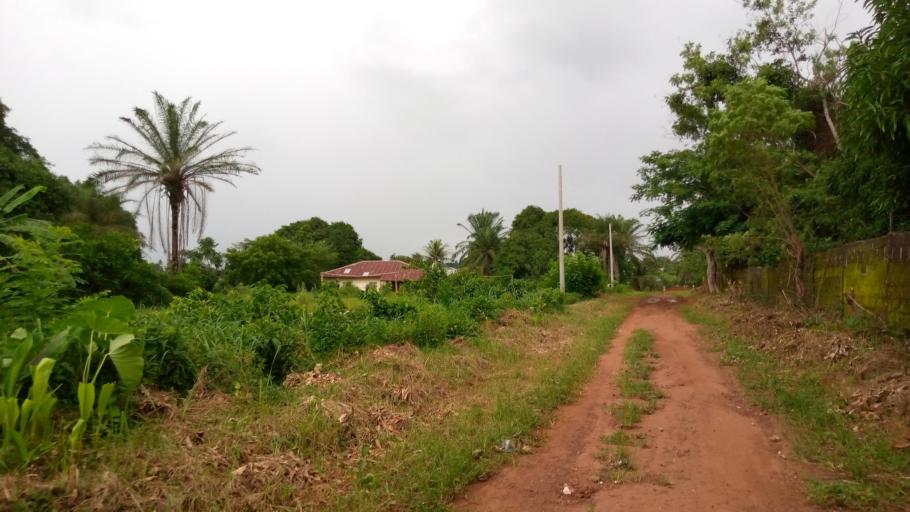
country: SL
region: Southern Province
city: Moyamba
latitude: 8.1588
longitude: -12.4370
